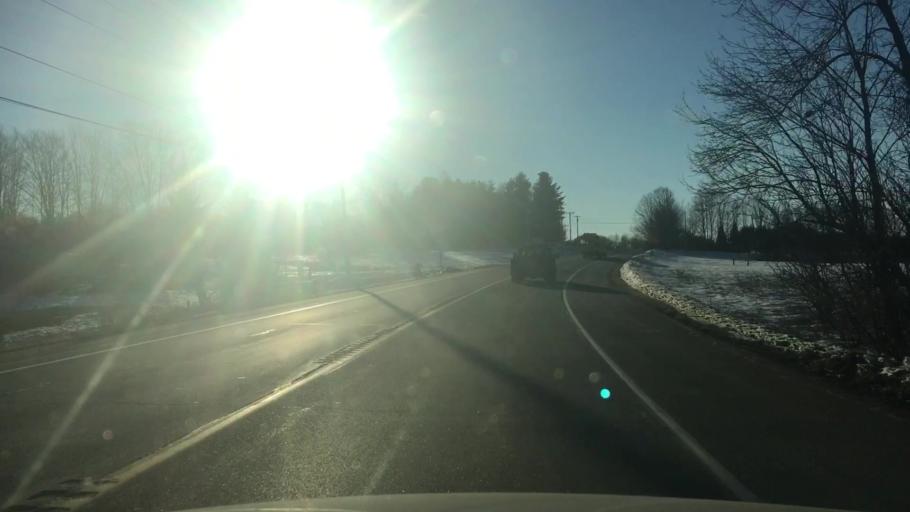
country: US
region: Maine
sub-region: Somerset County
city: Skowhegan
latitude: 44.7428
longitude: -69.7463
